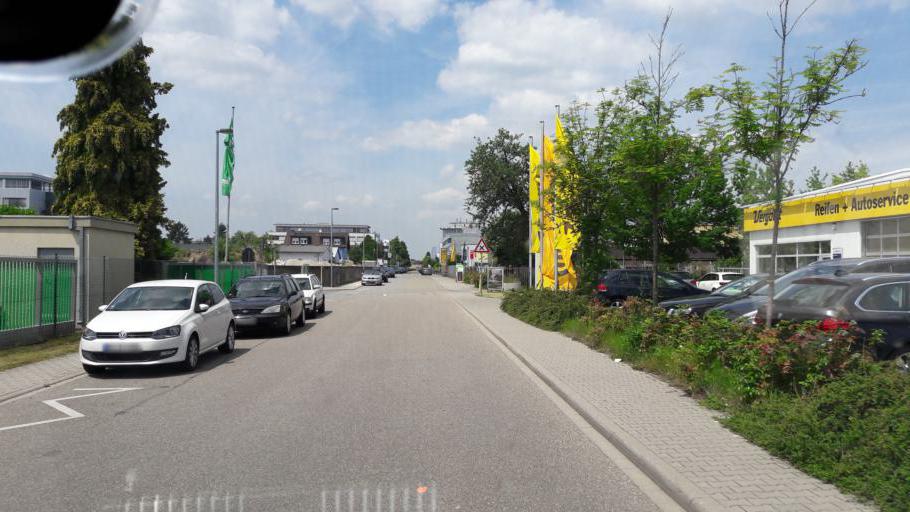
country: DE
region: Baden-Wuerttemberg
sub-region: Karlsruhe Region
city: Walldorf
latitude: 49.2925
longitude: 8.6517
